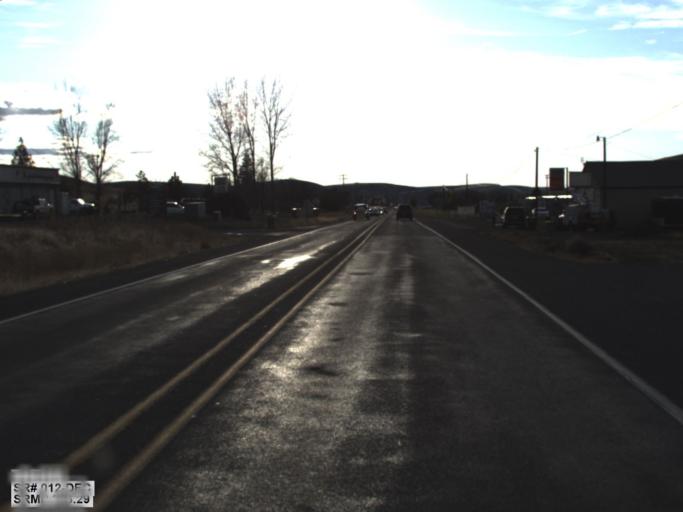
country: US
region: Washington
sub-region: Columbia County
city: Dayton
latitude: 46.3114
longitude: -117.9933
